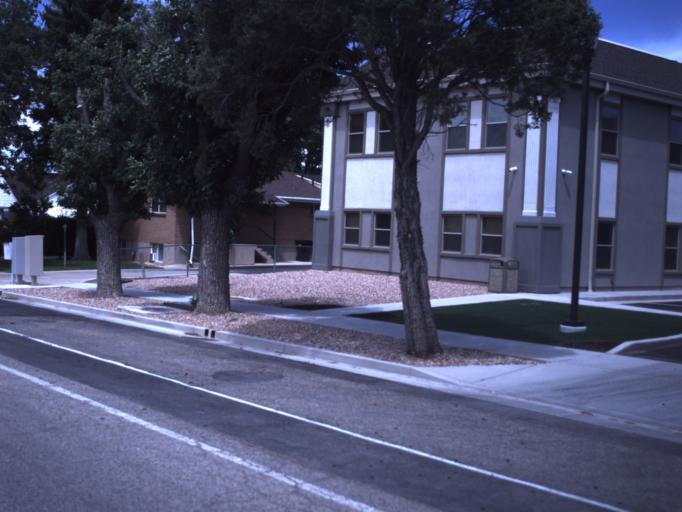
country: US
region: Utah
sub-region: Iron County
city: Cedar City
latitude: 37.6792
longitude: -113.0669
